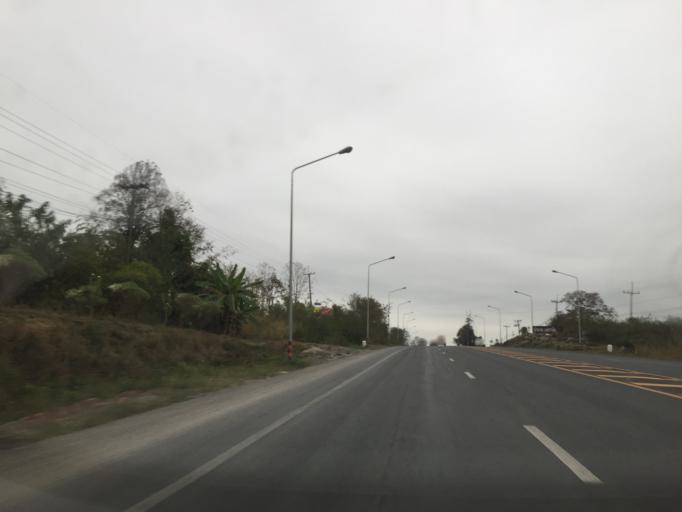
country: TH
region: Loei
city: Erawan
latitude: 17.3159
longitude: 101.9304
